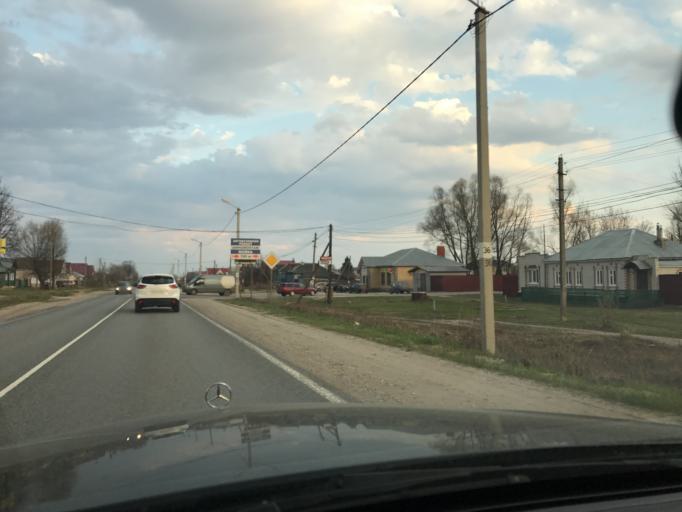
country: RU
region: Vladimir
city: Murom
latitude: 55.6092
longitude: 41.9541
